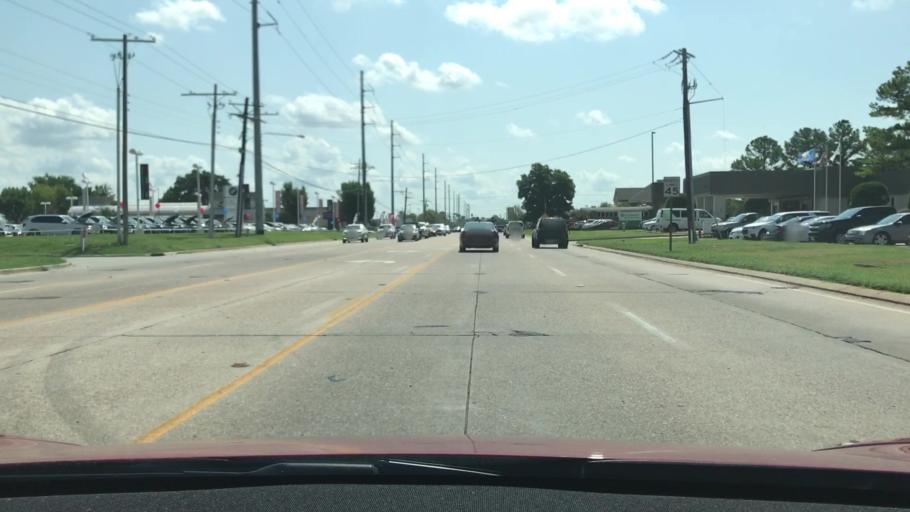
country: US
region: Louisiana
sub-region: Bossier Parish
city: Bossier City
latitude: 32.4434
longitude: -93.7270
